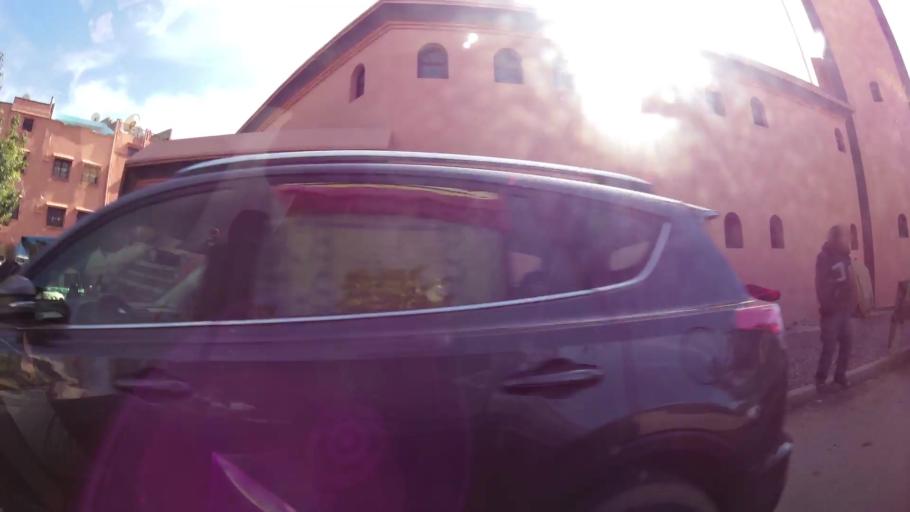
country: MA
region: Marrakech-Tensift-Al Haouz
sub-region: Marrakech
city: Marrakesh
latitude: 31.6510
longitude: -8.0238
